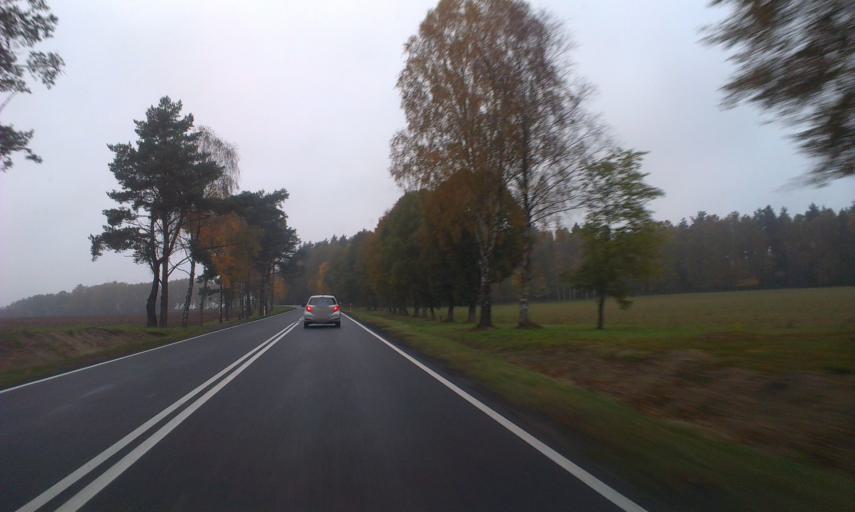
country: PL
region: West Pomeranian Voivodeship
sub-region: Powiat koszalinski
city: Bobolice
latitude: 54.0133
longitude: 16.5003
